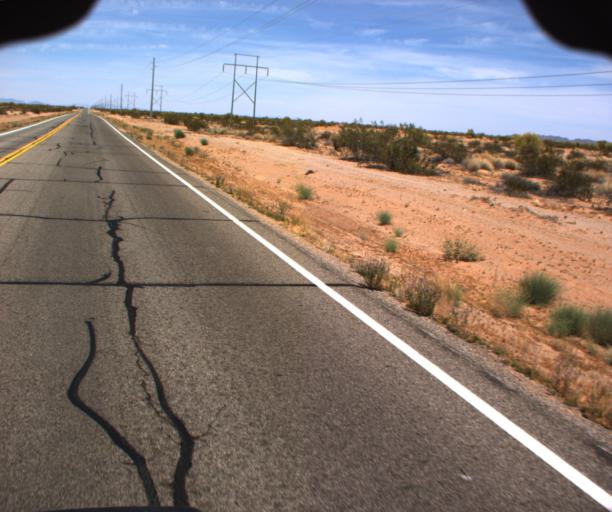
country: US
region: Arizona
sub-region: La Paz County
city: Quartzsite
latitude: 33.7884
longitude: -114.2170
